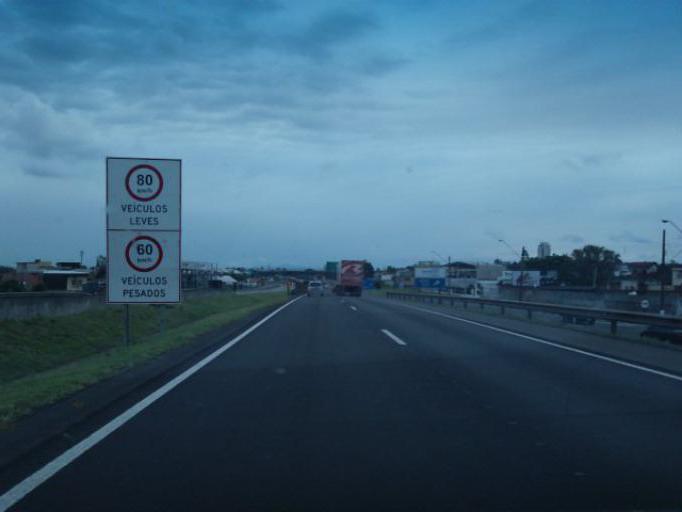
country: BR
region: Sao Paulo
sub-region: Registro
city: Registro
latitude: -24.4979
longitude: -47.8423
